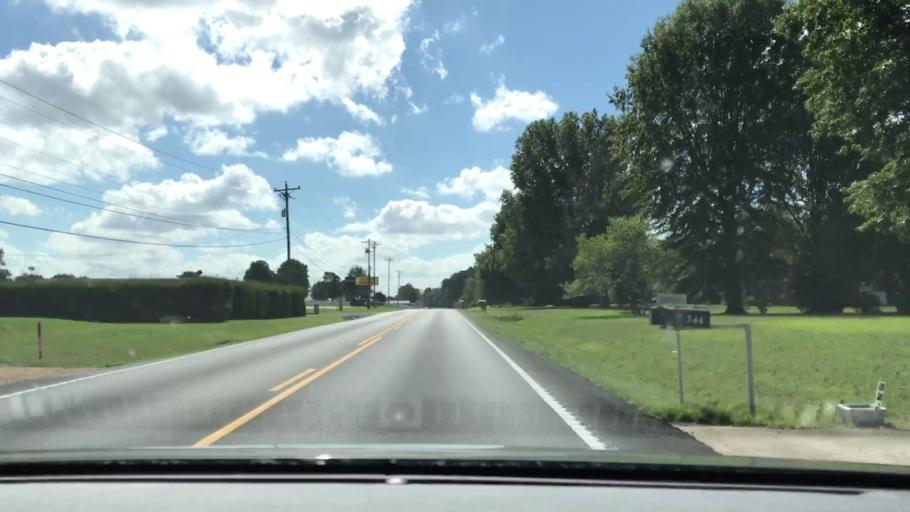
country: US
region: Kentucky
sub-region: Graves County
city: Mayfield
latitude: 36.7646
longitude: -88.5961
